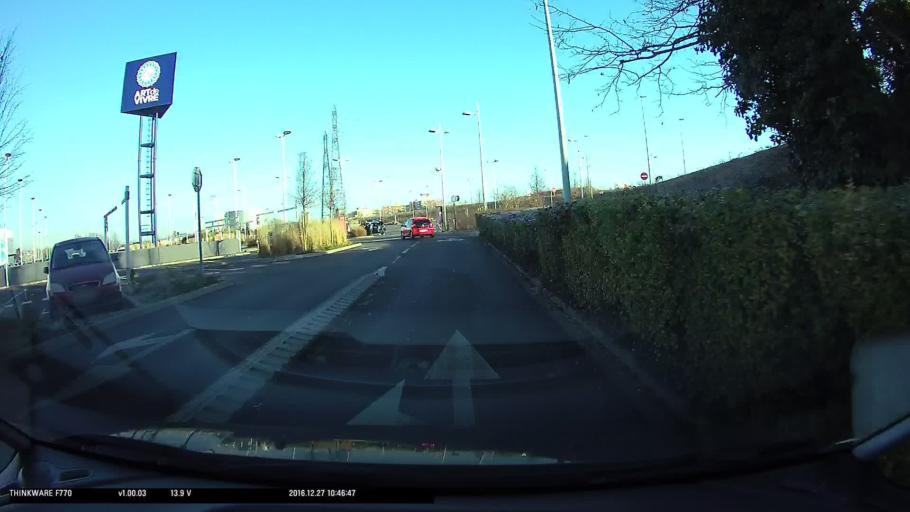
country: FR
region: Ile-de-France
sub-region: Departement du Val-d'Oise
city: Eragny
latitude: 49.0311
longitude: 2.1044
